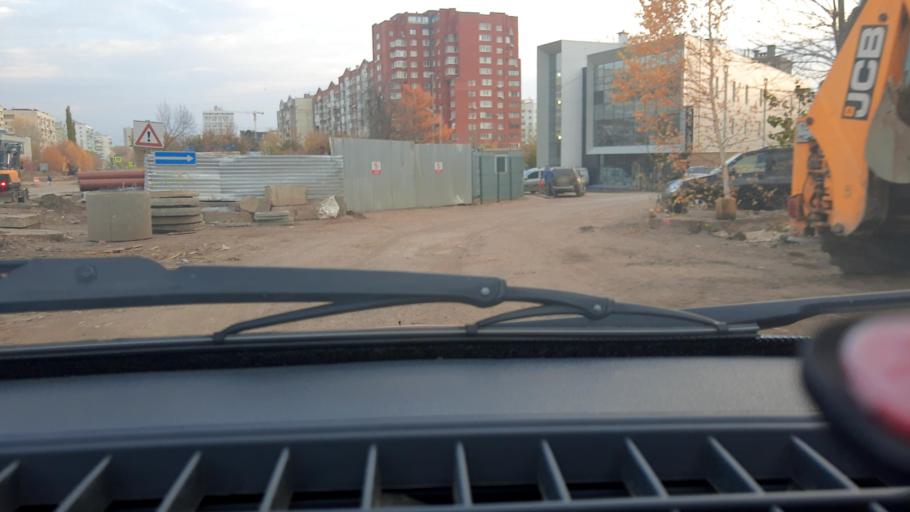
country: RU
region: Bashkortostan
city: Ufa
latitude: 54.7432
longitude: 55.9967
